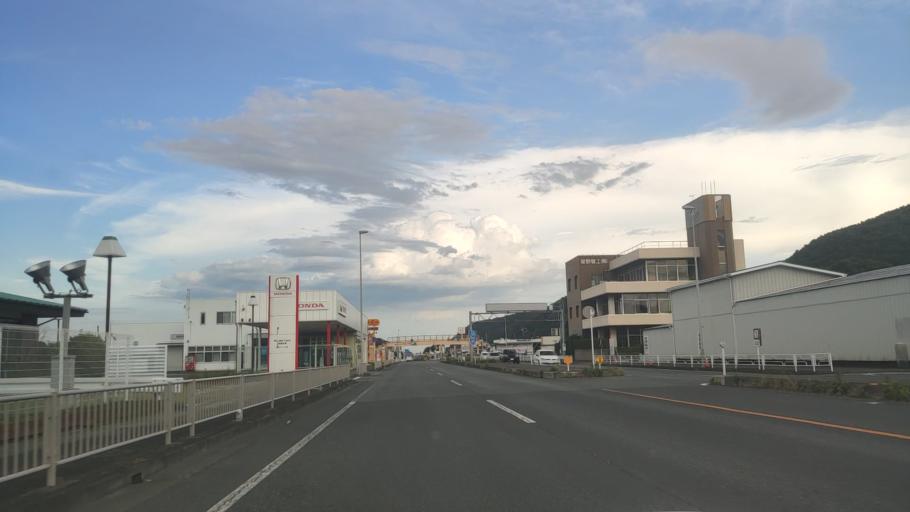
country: JP
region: Gunma
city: Kiryu
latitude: 36.3780
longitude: 139.3453
